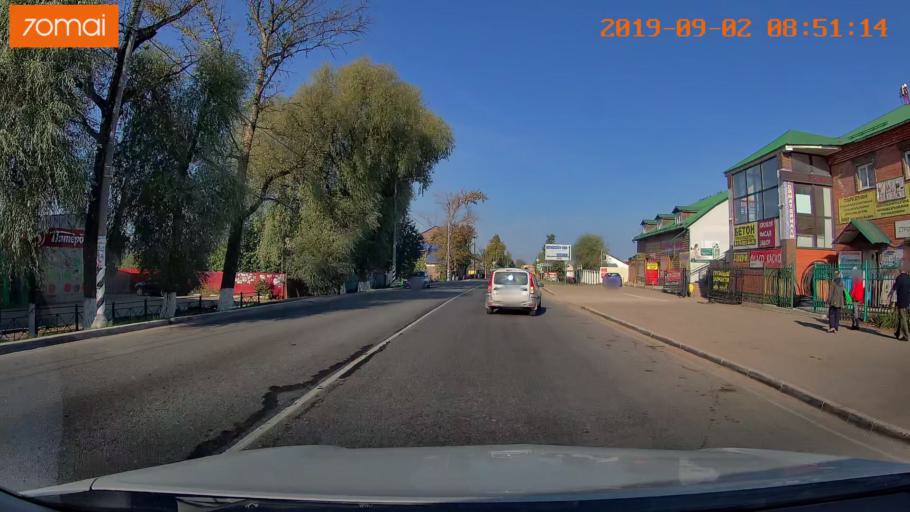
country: RU
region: Kaluga
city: Medyn'
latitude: 54.9653
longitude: 35.8735
